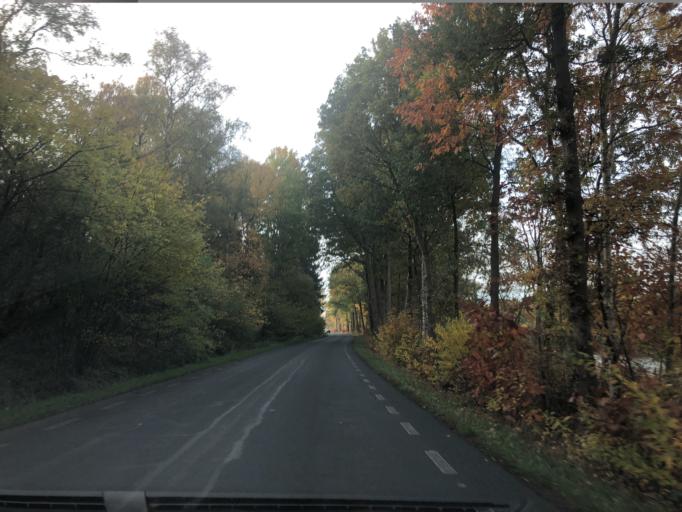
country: DE
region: Lower Saxony
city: Edewecht
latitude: 53.0837
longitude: 7.9849
